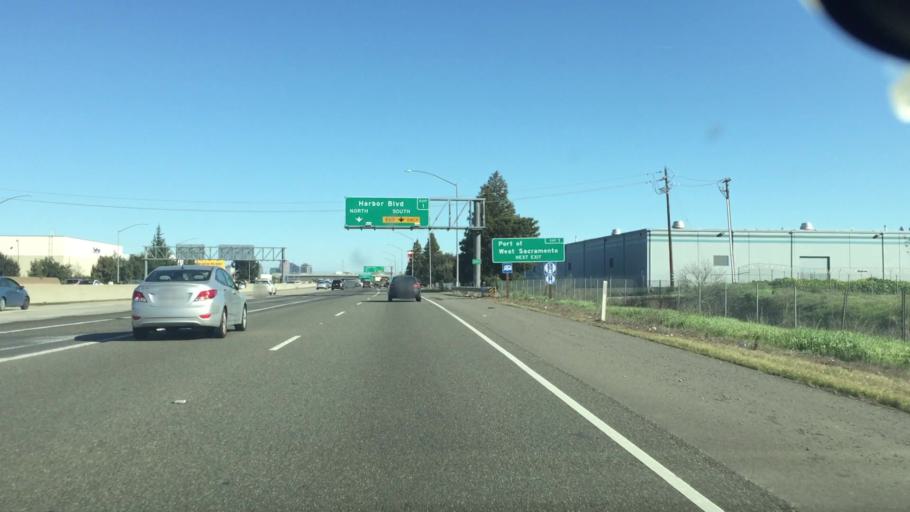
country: US
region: California
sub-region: Yolo County
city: West Sacramento
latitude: 38.5749
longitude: -121.5566
